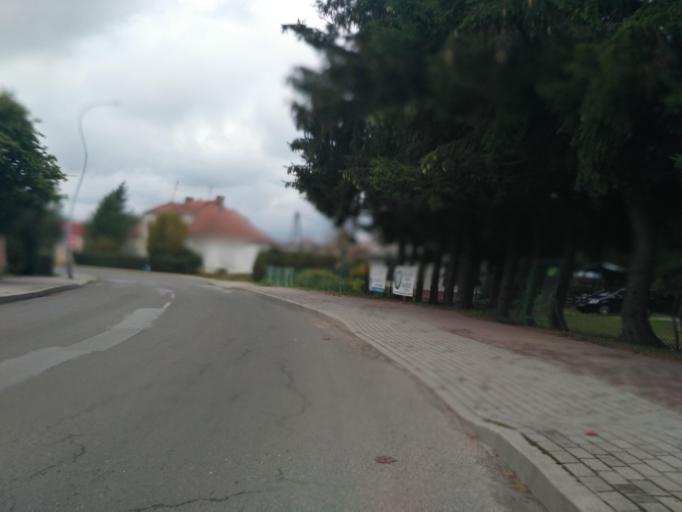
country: PL
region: Subcarpathian Voivodeship
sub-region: Krosno
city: Krosno
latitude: 49.6875
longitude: 21.7826
